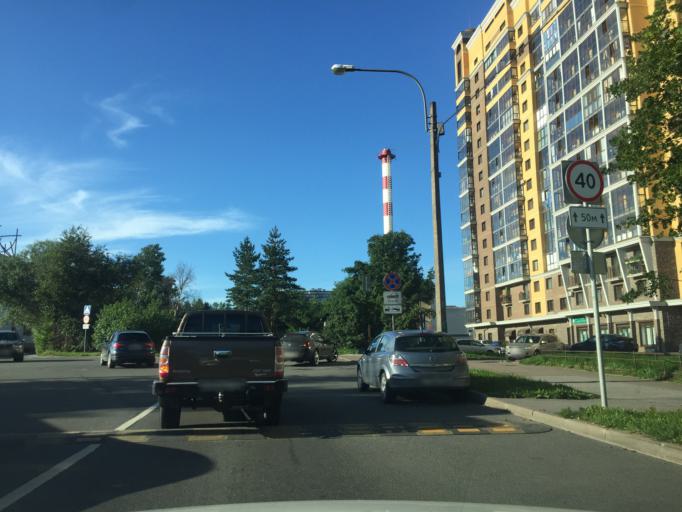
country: RU
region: St.-Petersburg
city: Admiralteisky
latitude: 59.8800
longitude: 30.3133
